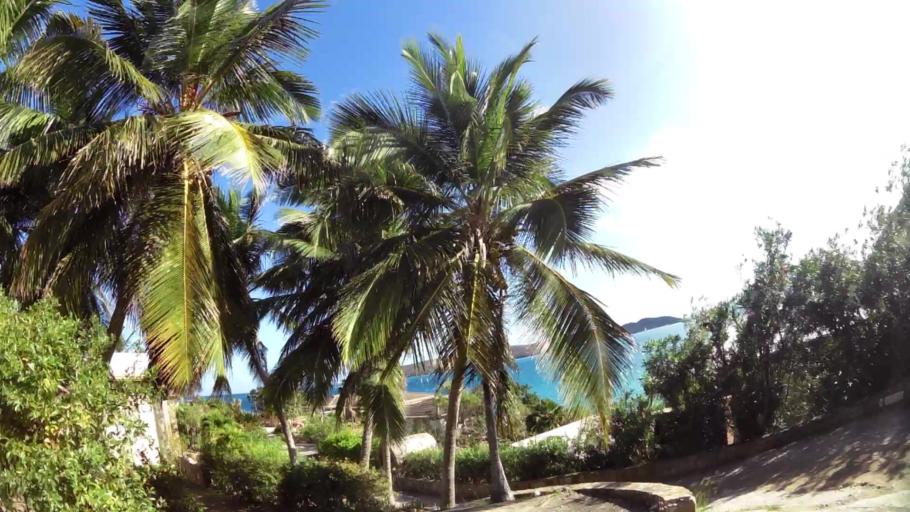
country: VG
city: Tortola
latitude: 18.4978
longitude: -64.3842
